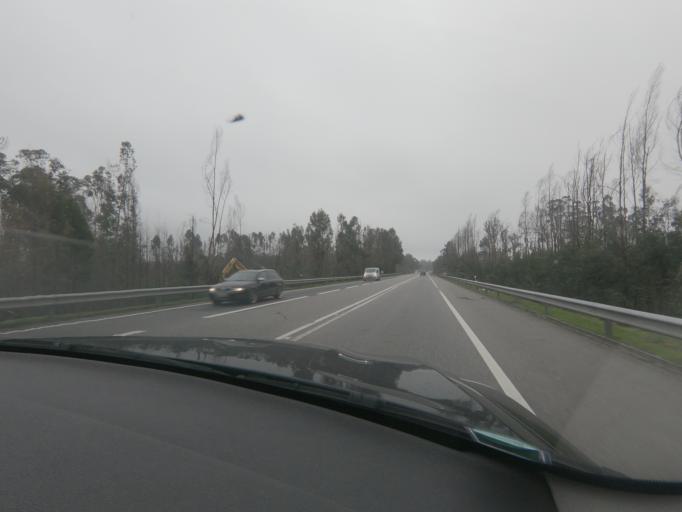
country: PT
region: Viseu
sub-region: Concelho de Tondela
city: Tondela
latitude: 40.5578
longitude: -8.0516
